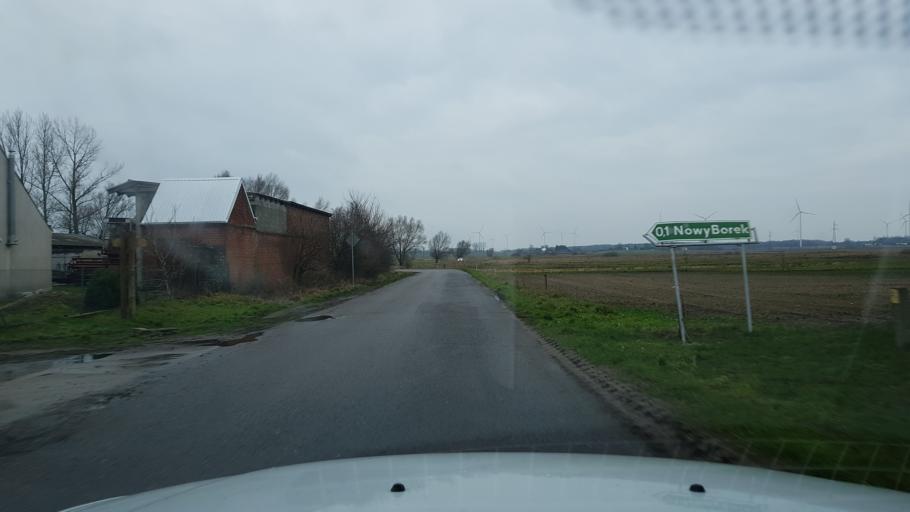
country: PL
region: West Pomeranian Voivodeship
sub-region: Powiat kolobrzeski
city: Grzybowo
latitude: 54.1305
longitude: 15.4690
